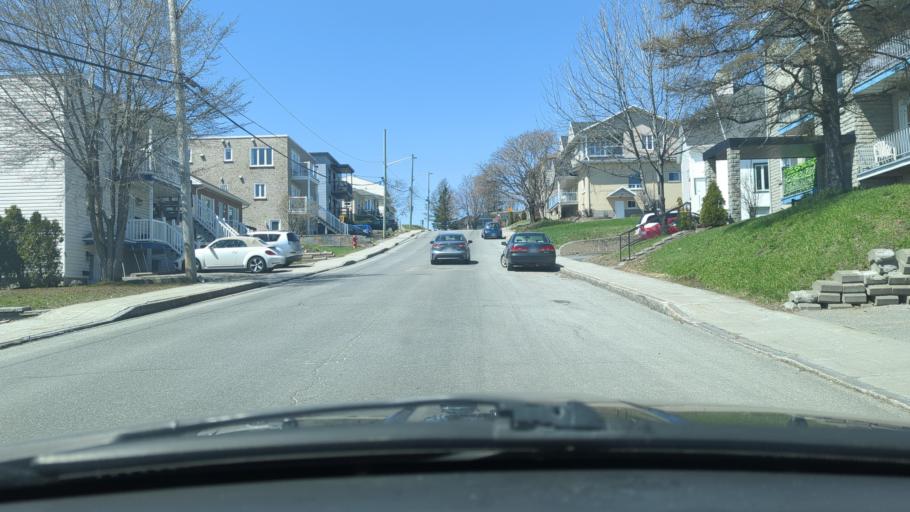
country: CA
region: Quebec
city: Quebec
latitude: 46.8555
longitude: -71.2064
